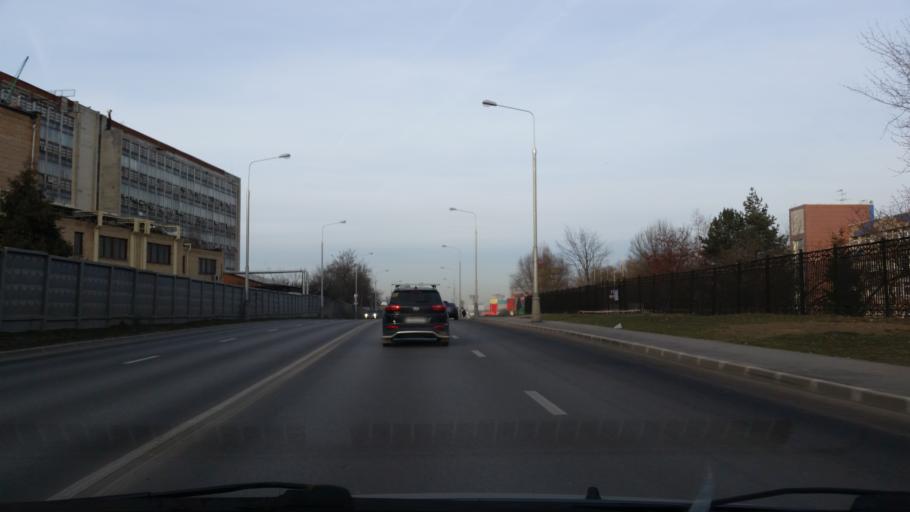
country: RU
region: Moscow
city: Nagornyy
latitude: 55.6283
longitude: 37.6222
